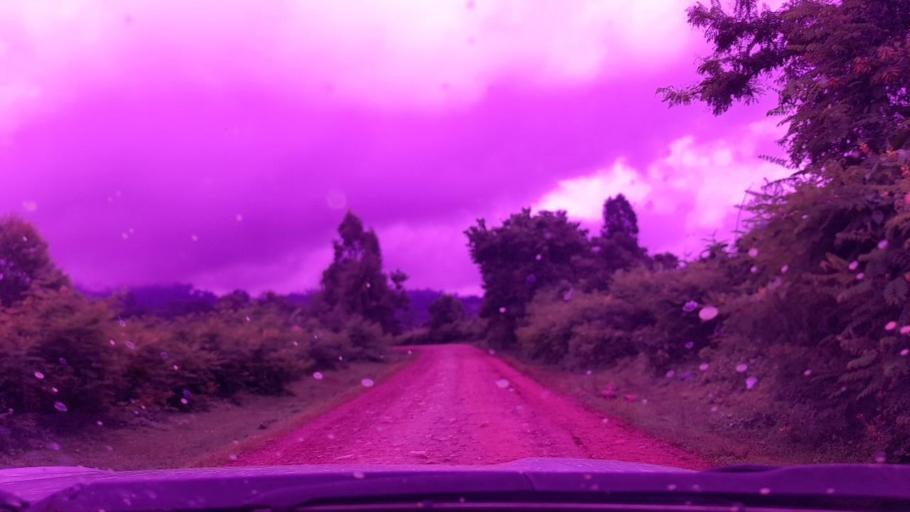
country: ET
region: Southern Nations, Nationalities, and People's Region
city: Bonga
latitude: 7.5584
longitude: 35.8409
